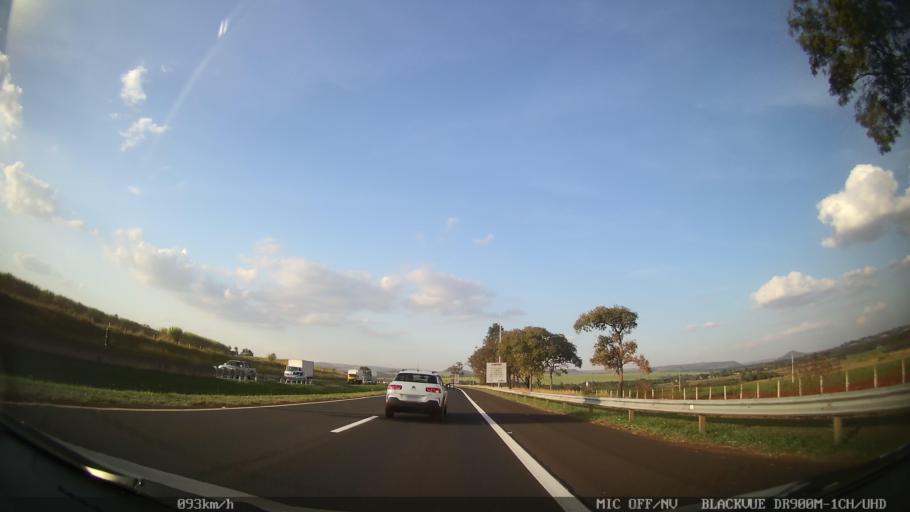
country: BR
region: Sao Paulo
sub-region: Ribeirao Preto
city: Ribeirao Preto
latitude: -21.1088
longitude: -47.7720
